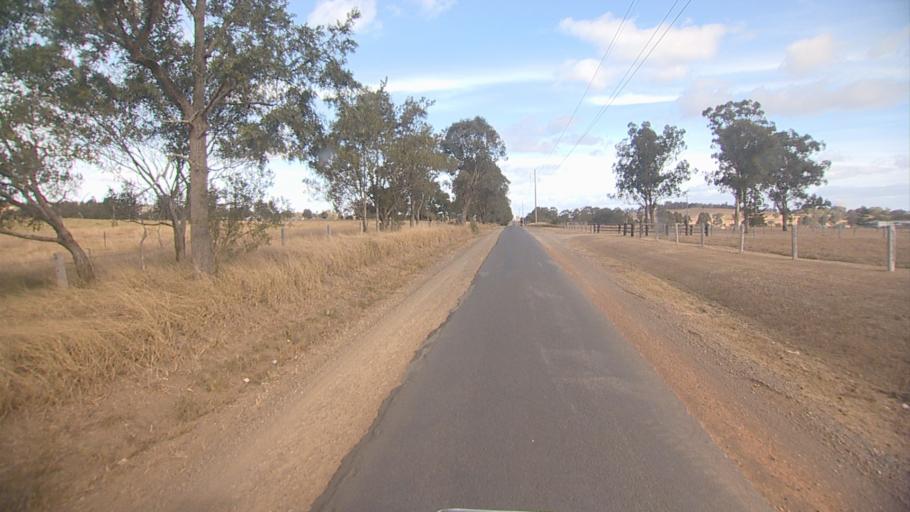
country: AU
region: Queensland
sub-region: Logan
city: Cedar Vale
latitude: -27.9153
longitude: 153.0137
